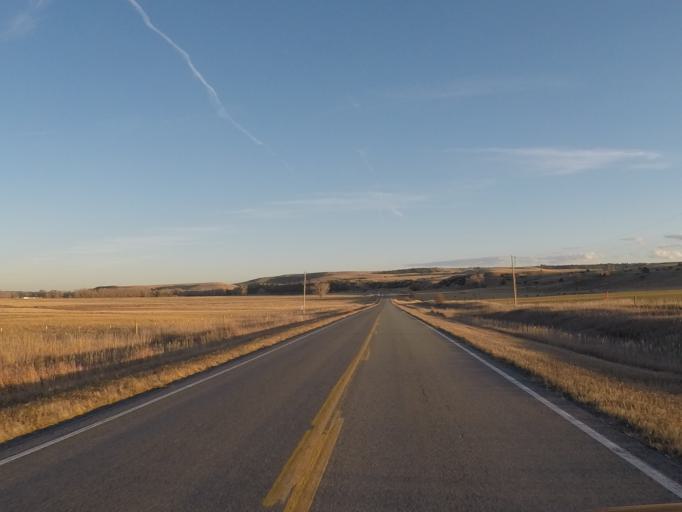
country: US
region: Montana
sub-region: Sweet Grass County
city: Big Timber
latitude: 45.7939
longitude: -109.8564
